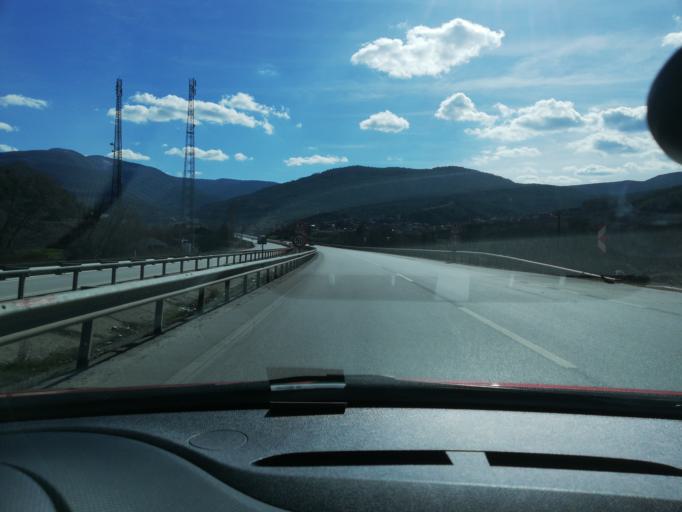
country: TR
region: Karabuk
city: Karabuk
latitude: 41.1104
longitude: 32.6690
